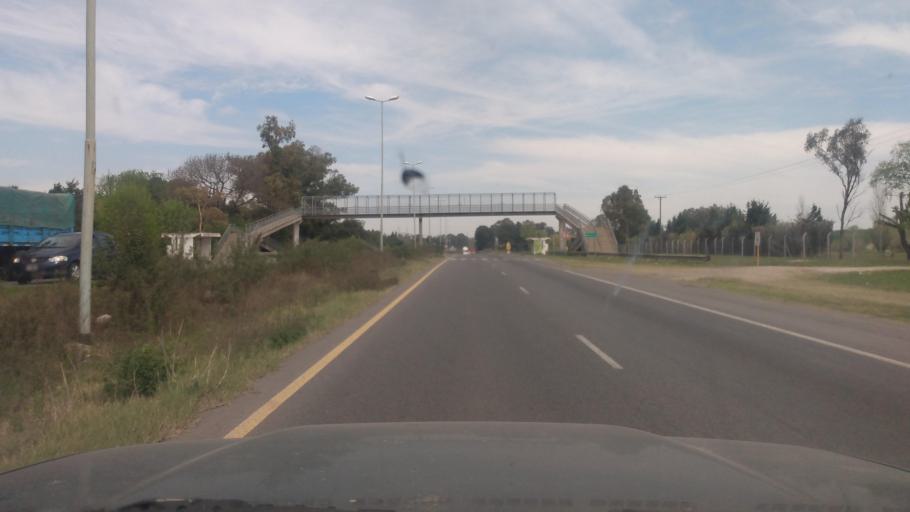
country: AR
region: Buenos Aires
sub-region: Partido de Lujan
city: Lujan
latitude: -34.4462
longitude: -59.0515
